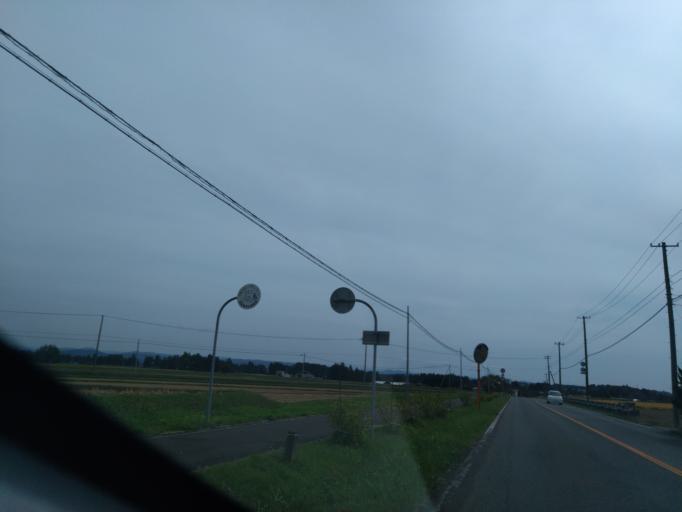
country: JP
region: Iwate
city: Hanamaki
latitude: 39.4325
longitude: 141.0831
